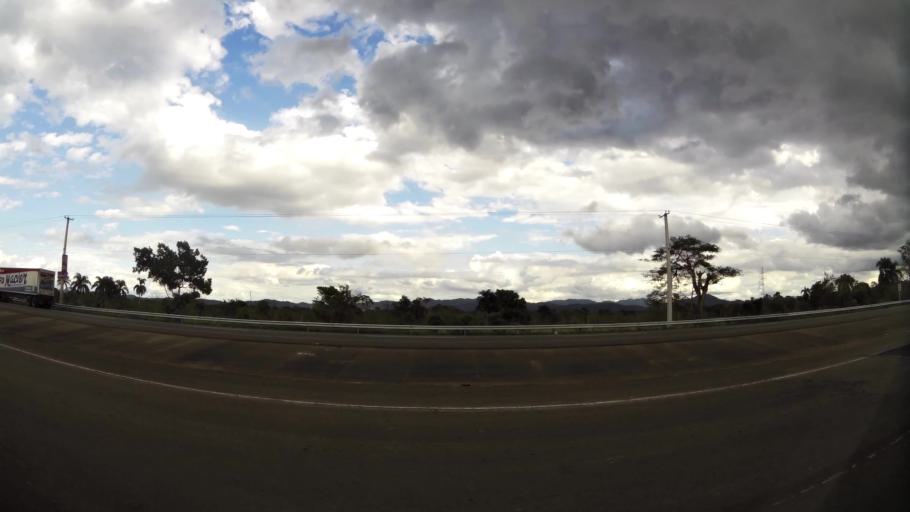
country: DO
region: Monsenor Nouel
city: Sabana del Puerto
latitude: 19.0586
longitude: -70.4463
